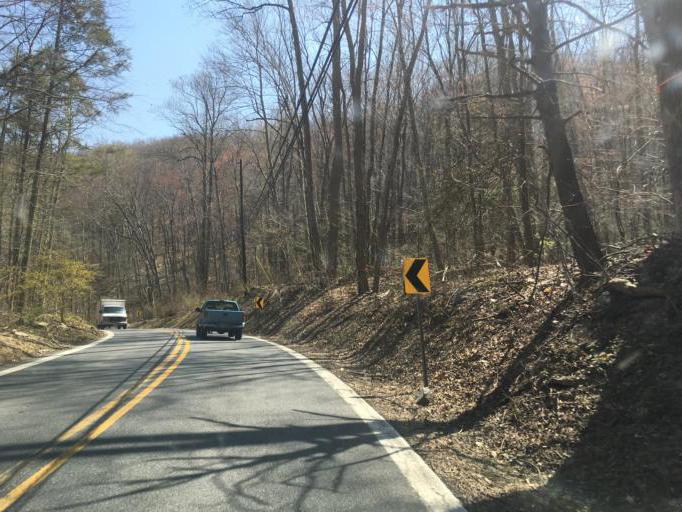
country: US
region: Maryland
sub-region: Frederick County
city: Thurmont
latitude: 39.6221
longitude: -77.4386
